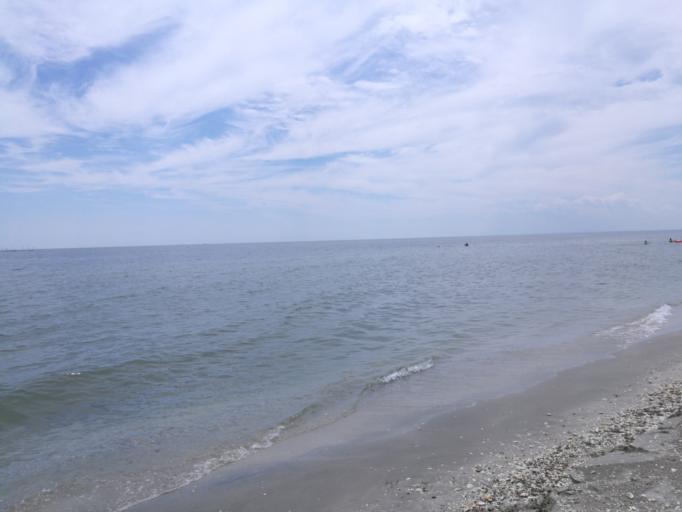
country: RO
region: Constanta
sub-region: Comuna Corbu
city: Corbu
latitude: 44.4269
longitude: 28.7642
